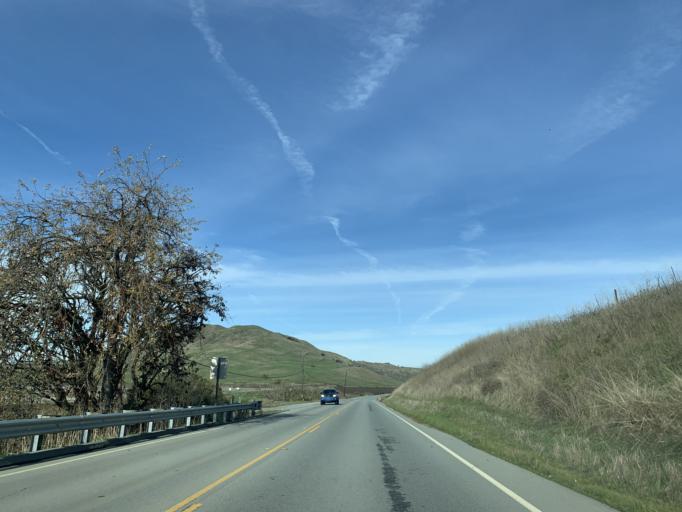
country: US
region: California
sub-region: San Benito County
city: Ridgemark
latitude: 36.7220
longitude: -121.2789
